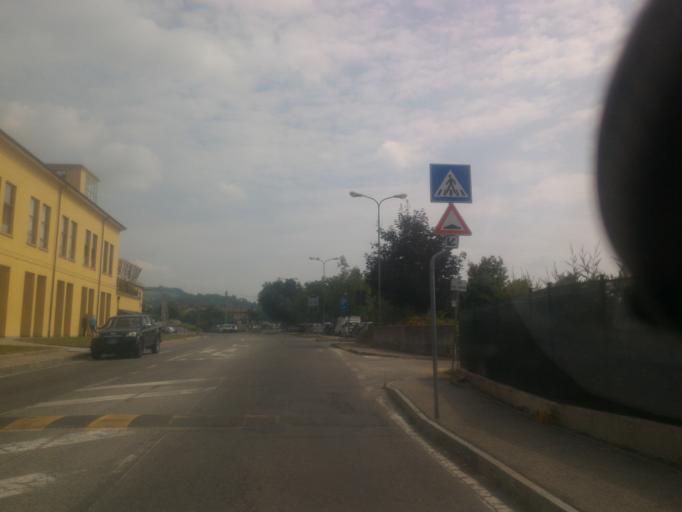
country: IT
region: Piedmont
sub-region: Provincia di Torino
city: San Secondo di Pinerolo
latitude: 44.8768
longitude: 7.3124
